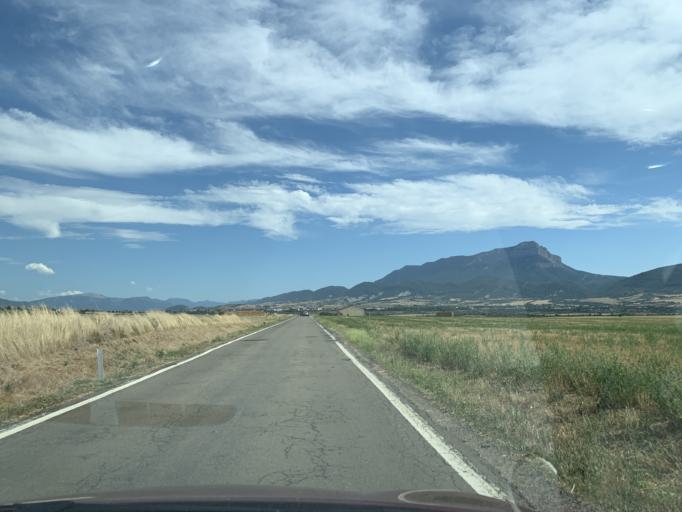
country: ES
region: Aragon
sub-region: Provincia de Huesca
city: Jaca
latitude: 42.5851
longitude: -0.6005
